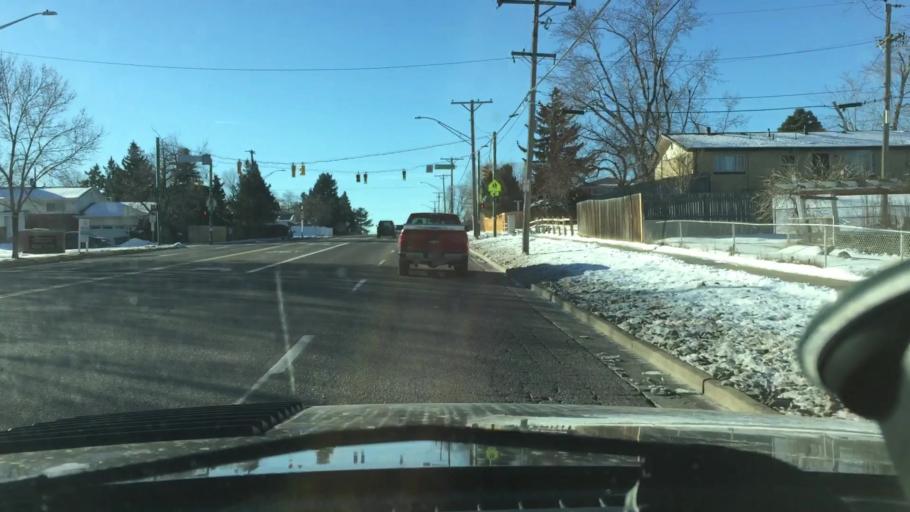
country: US
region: Colorado
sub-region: Adams County
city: Northglenn
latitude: 39.8791
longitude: -104.9967
